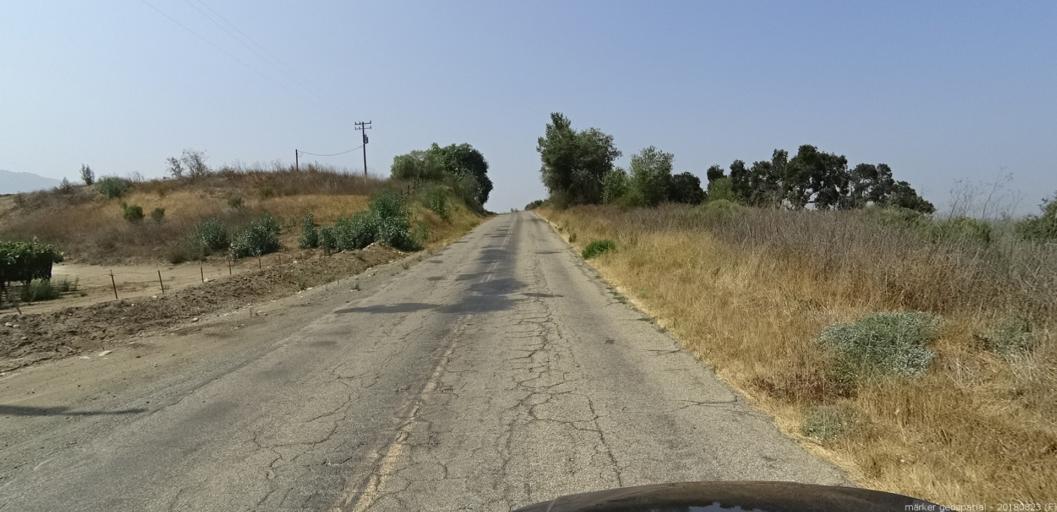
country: US
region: California
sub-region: Monterey County
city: Gonzales
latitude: 36.4481
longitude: -121.4343
